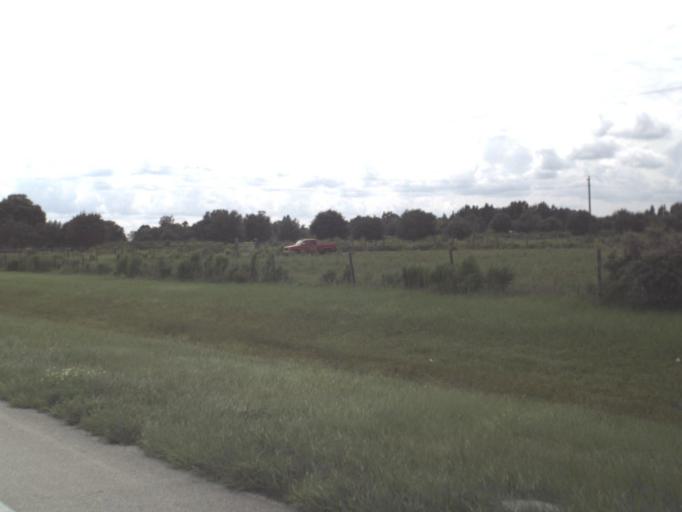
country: US
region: Florida
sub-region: DeSoto County
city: Southeast Arcadia
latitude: 27.1210
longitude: -81.7950
